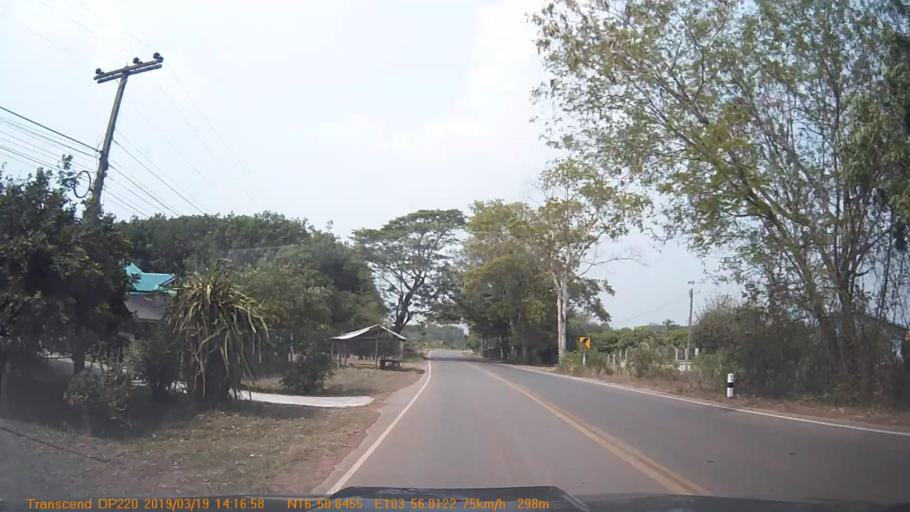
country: TH
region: Kalasin
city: Na Khu
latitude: 16.8476
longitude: 103.9470
